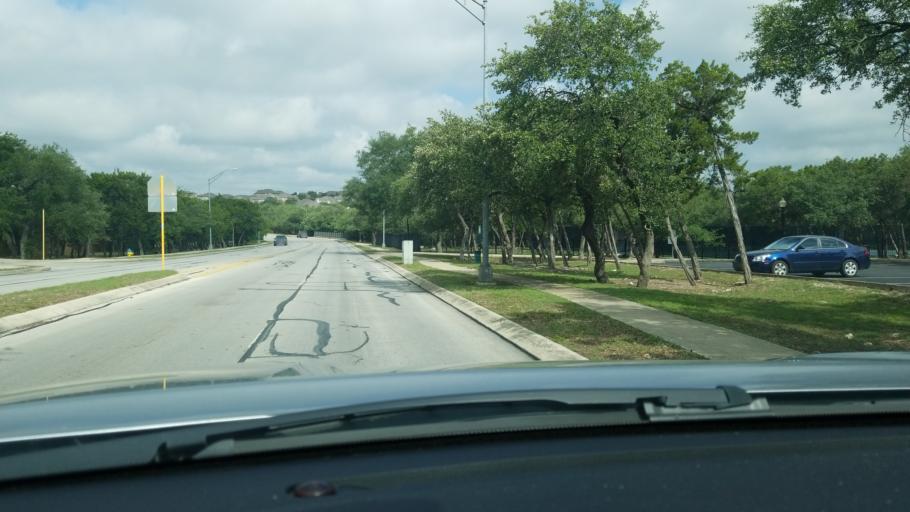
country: US
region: Texas
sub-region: Bexar County
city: Timberwood Park
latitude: 29.6859
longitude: -98.4615
